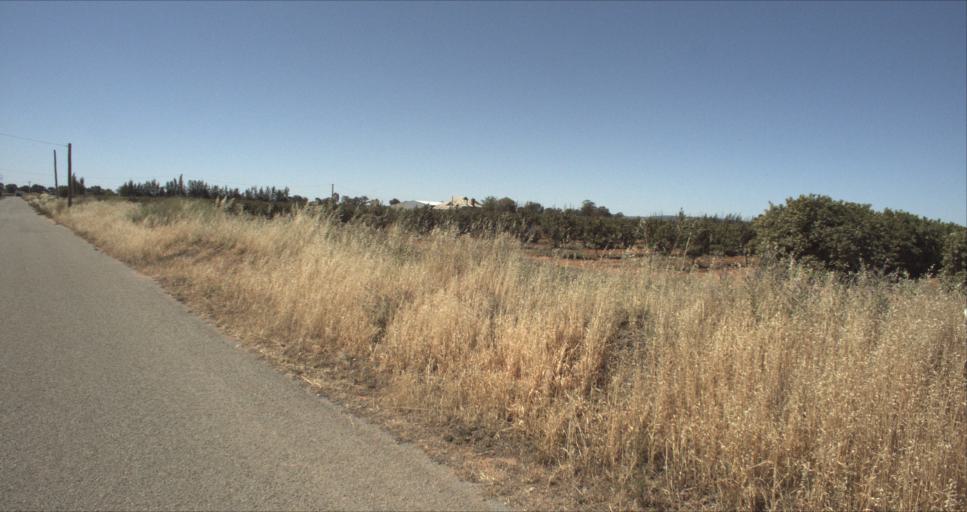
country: AU
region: New South Wales
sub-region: Leeton
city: Leeton
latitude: -34.5372
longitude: 146.3522
